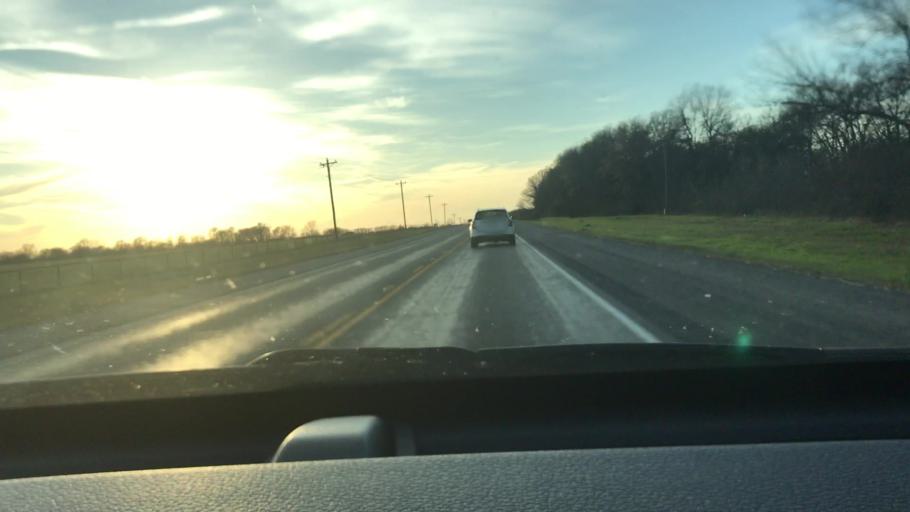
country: US
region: Texas
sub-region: Red River County
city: Clarksville
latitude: 33.6061
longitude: -95.0012
